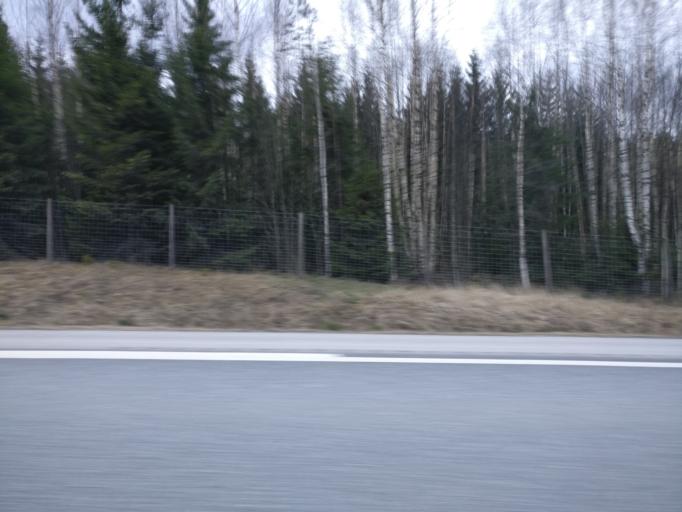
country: FI
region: Haeme
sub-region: Haemeenlinna
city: Janakkala
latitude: 60.8572
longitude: 24.5919
